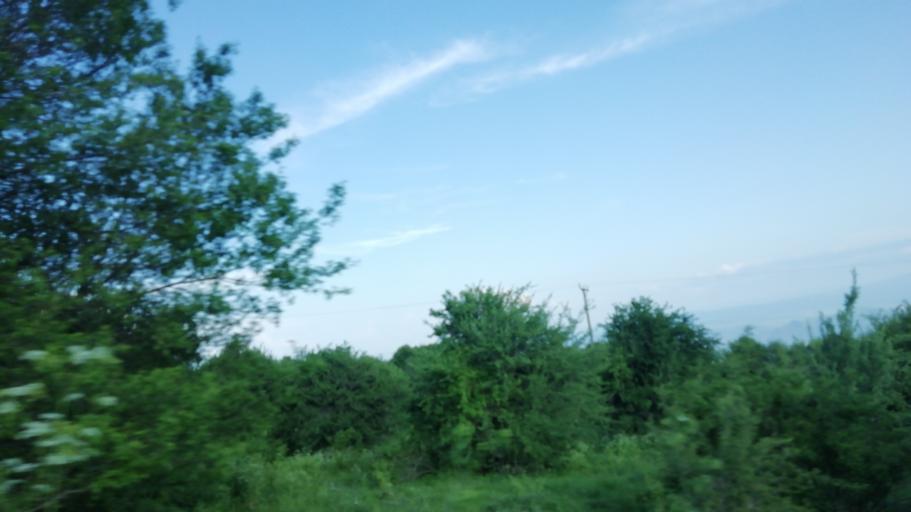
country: TR
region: Karabuk
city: Eskipazar
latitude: 41.0464
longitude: 32.5587
